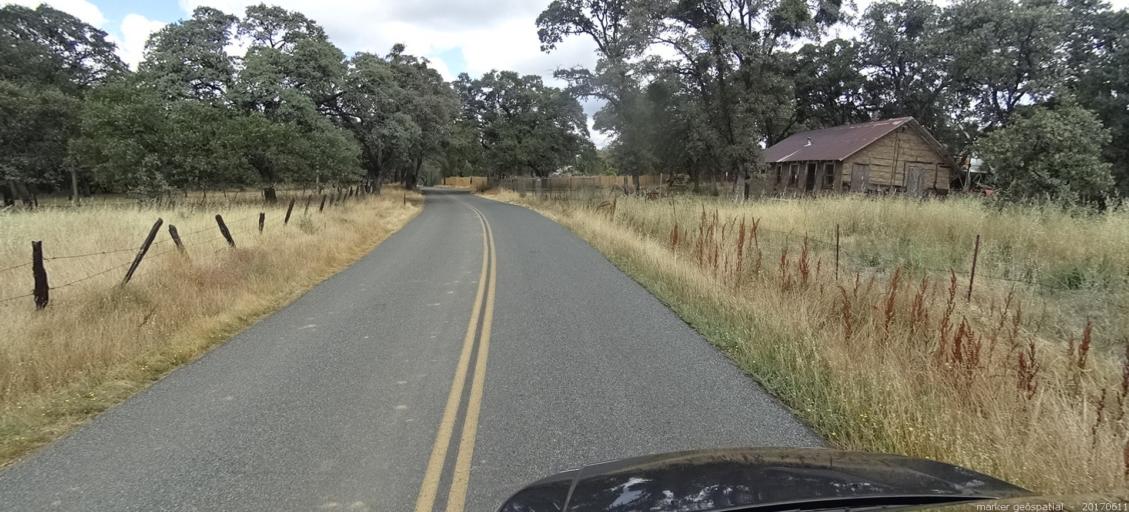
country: US
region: California
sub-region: Butte County
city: Oroville
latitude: 39.6153
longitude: -121.5260
